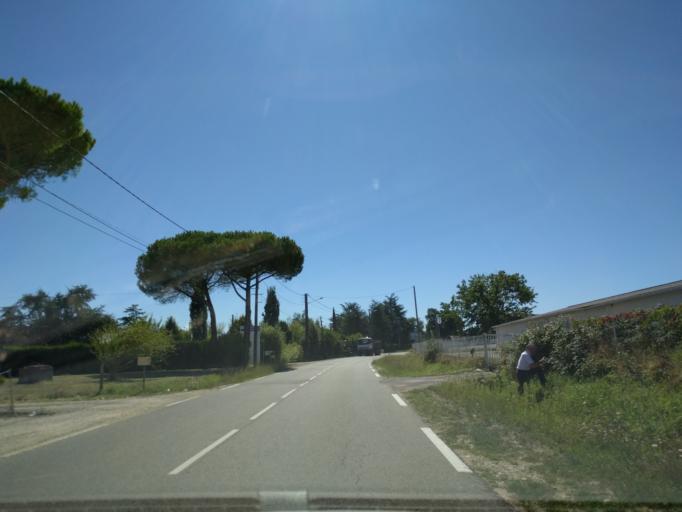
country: FR
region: Midi-Pyrenees
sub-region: Departement du Tarn-et-Garonne
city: Montauban
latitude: 44.0266
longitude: 1.3805
